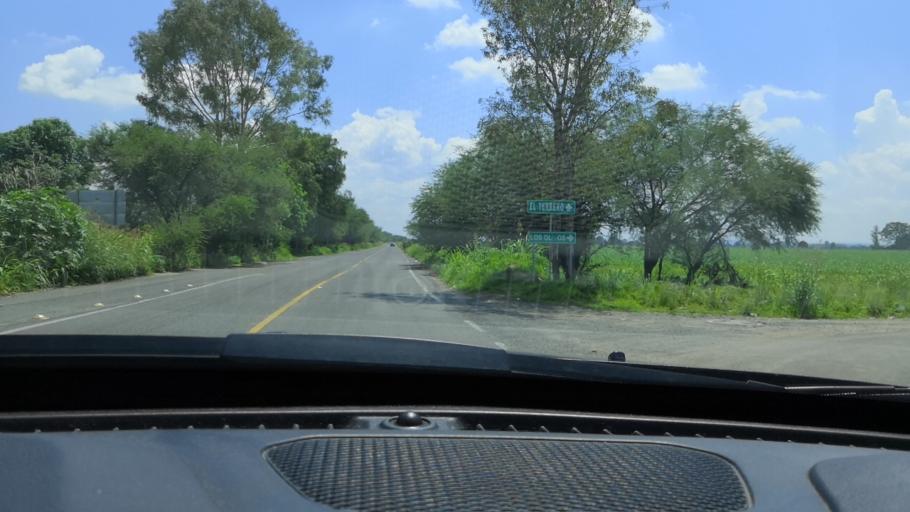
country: MX
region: Guanajuato
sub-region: Silao de la Victoria
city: El Refugio de los Sauces
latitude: 20.9577
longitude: -101.5914
